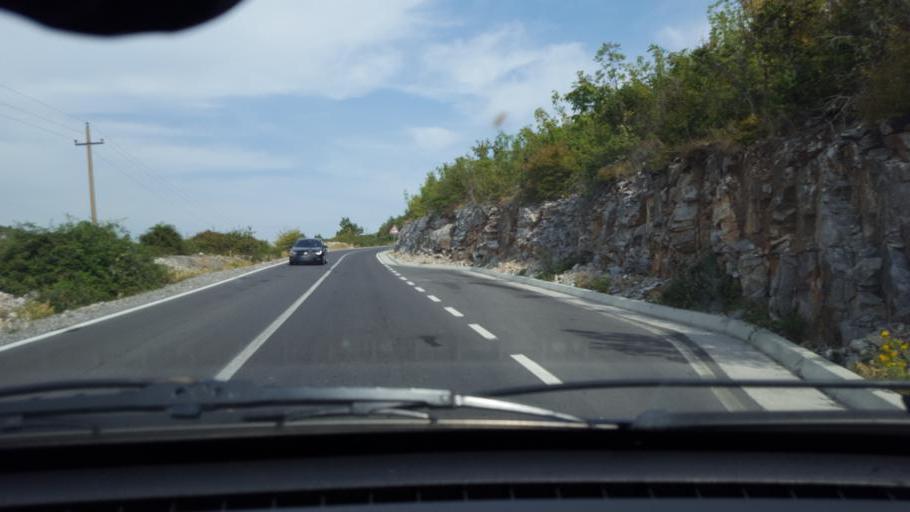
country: AL
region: Shkoder
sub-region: Rrethi i Malesia e Madhe
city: Kastrat
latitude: 42.3780
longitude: 19.4874
